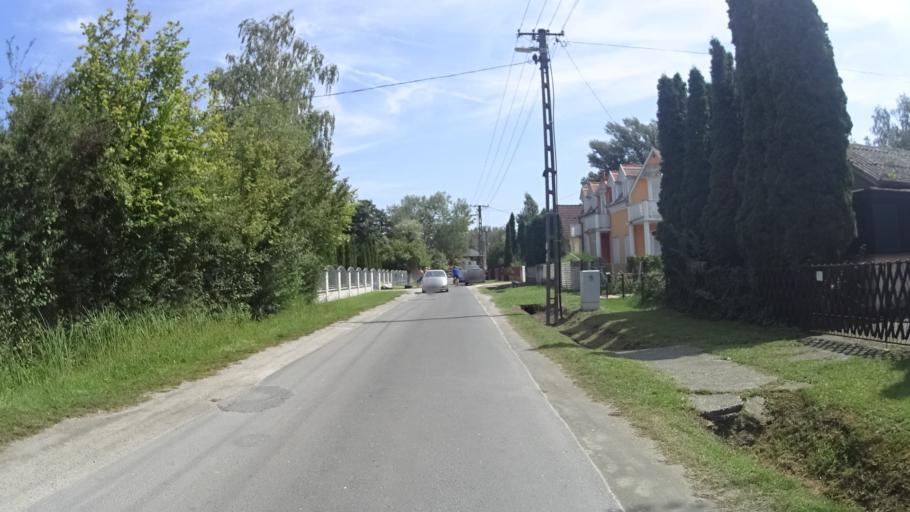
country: HU
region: Somogy
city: Balatonfenyves
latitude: 46.7086
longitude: 17.4524
